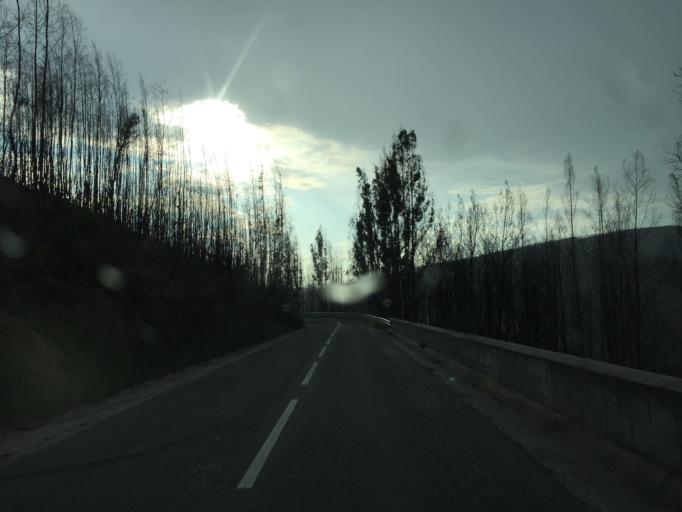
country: PT
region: Coimbra
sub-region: Pampilhosa da Serra
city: Pampilhosa da Serra
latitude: 40.0434
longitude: -7.9035
